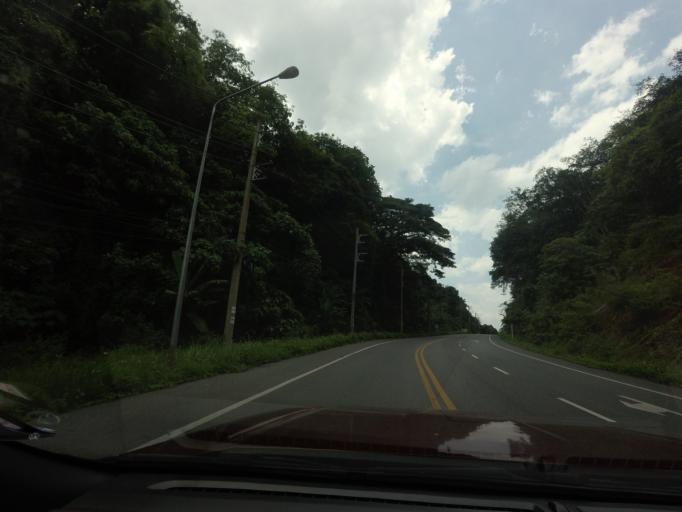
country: TH
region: Yala
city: Than To
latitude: 6.0620
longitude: 101.1942
